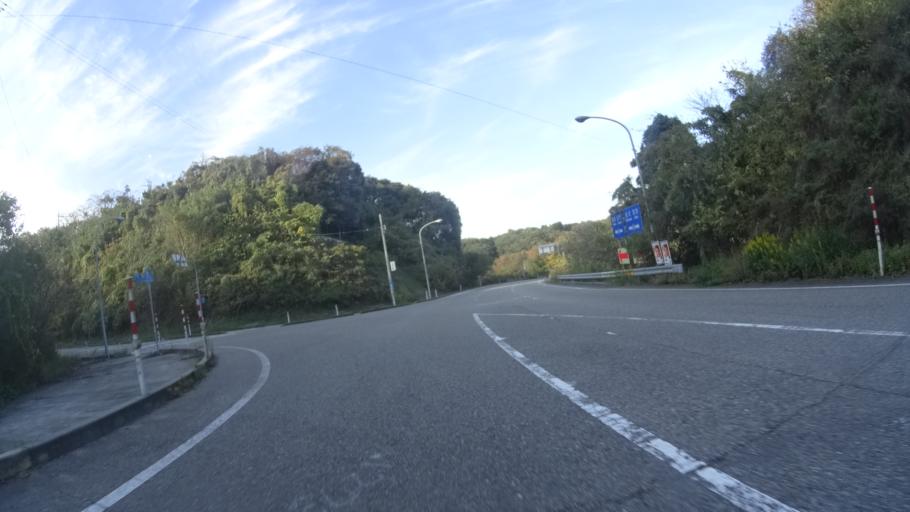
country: JP
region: Ishikawa
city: Hakui
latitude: 37.0775
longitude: 136.7294
